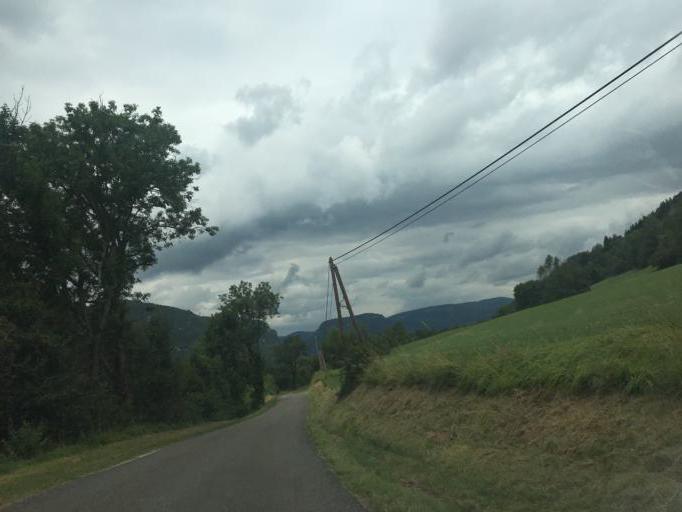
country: FR
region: Franche-Comte
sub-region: Departement du Jura
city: Saint-Claude
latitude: 46.3459
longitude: 5.8465
